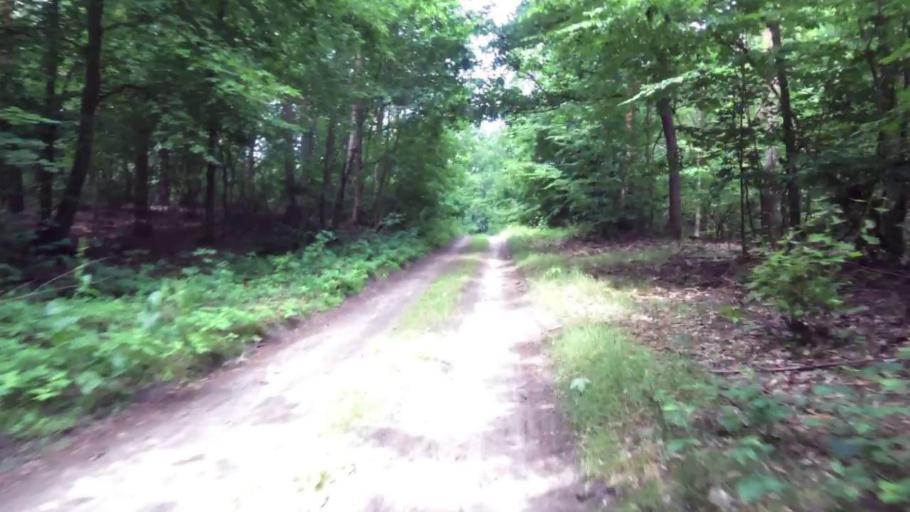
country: PL
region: West Pomeranian Voivodeship
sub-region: Powiat pyrzycki
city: Lipiany
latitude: 52.9852
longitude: 14.9099
